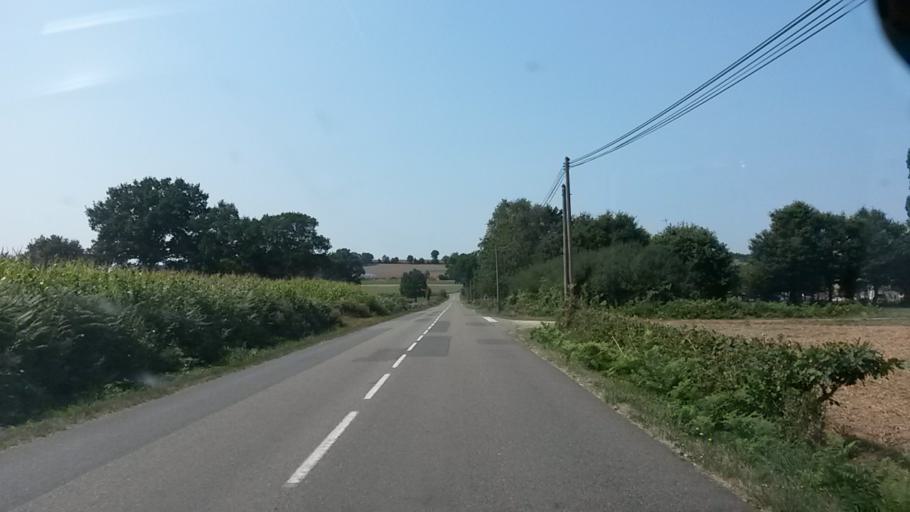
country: FR
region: Pays de la Loire
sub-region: Departement de la Mayenne
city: Saint-Pierre-des-Nids
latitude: 48.3676
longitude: -0.1514
